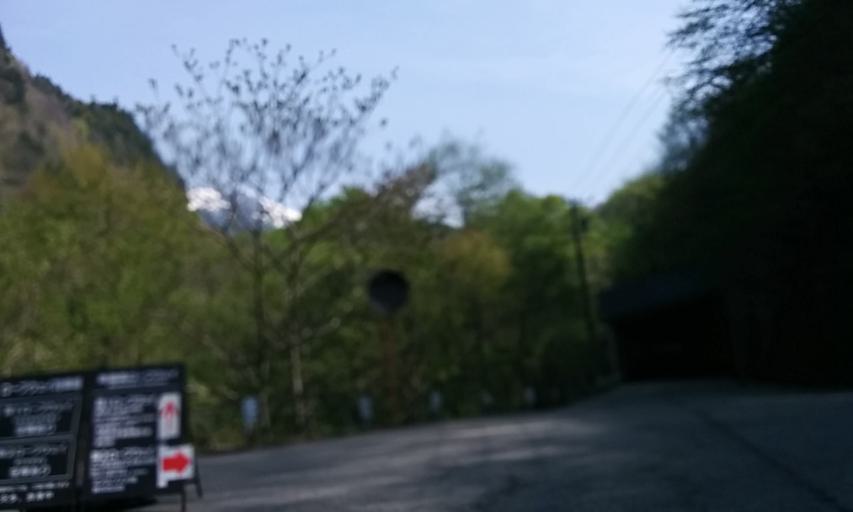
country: JP
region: Nagano
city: Hotaka
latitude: 36.2711
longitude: 137.5697
